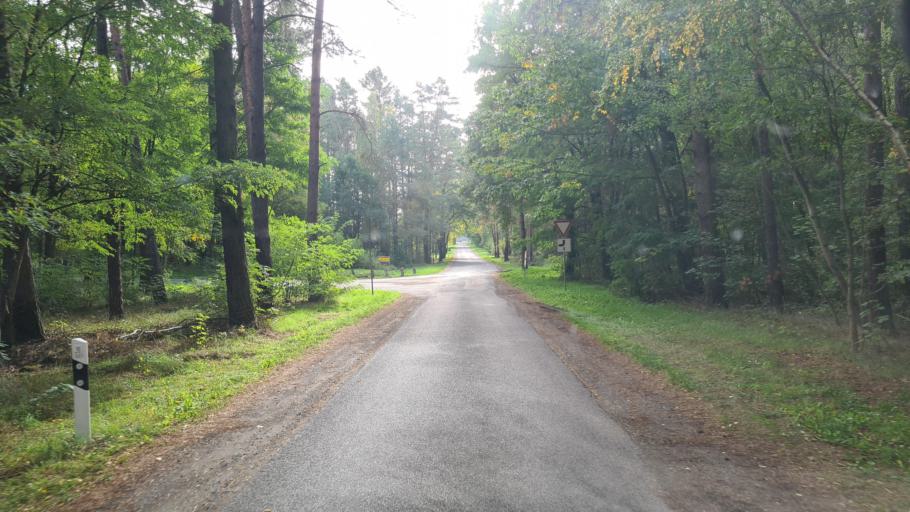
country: DE
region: Brandenburg
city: Linthe
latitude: 52.1016
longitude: 12.7567
